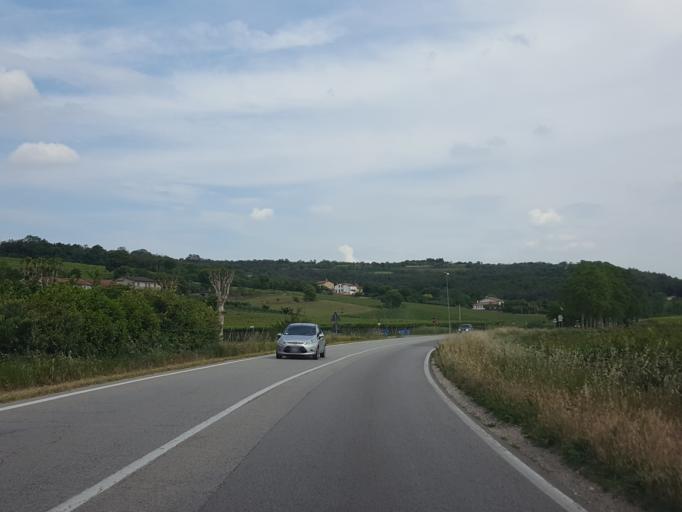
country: IT
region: Veneto
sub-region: Provincia di Vicenza
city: Alonte
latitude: 45.3578
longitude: 11.4350
